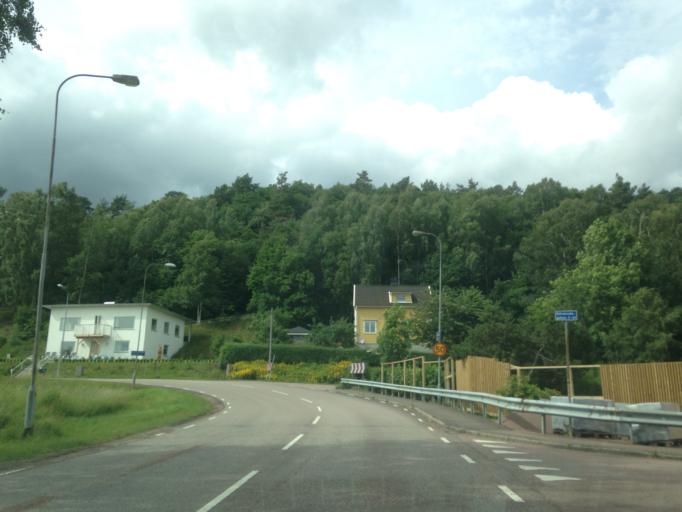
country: SE
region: Vaestra Goetaland
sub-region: Ale Kommun
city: Surte
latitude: 57.7891
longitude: 11.9783
